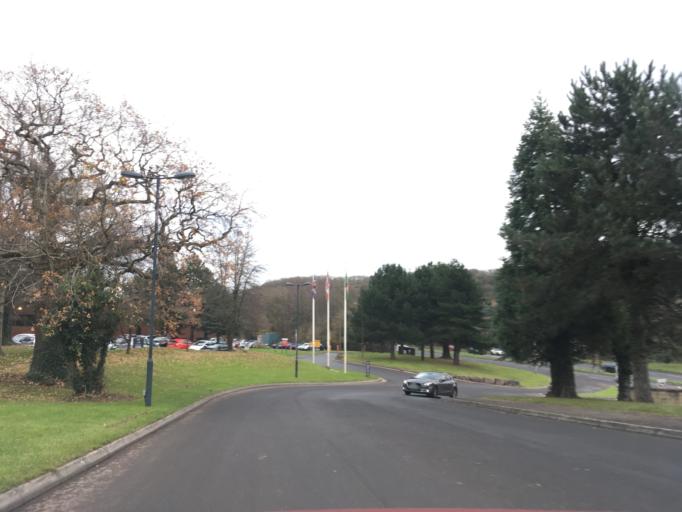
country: GB
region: Wales
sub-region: Newport
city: Langstone
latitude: 51.6006
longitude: -2.9310
